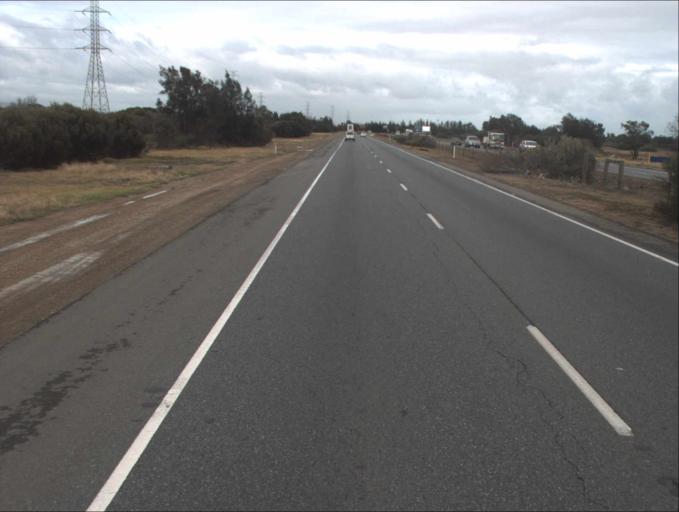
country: AU
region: South Australia
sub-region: Port Adelaide Enfield
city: Enfield
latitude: -34.8255
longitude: 138.5863
